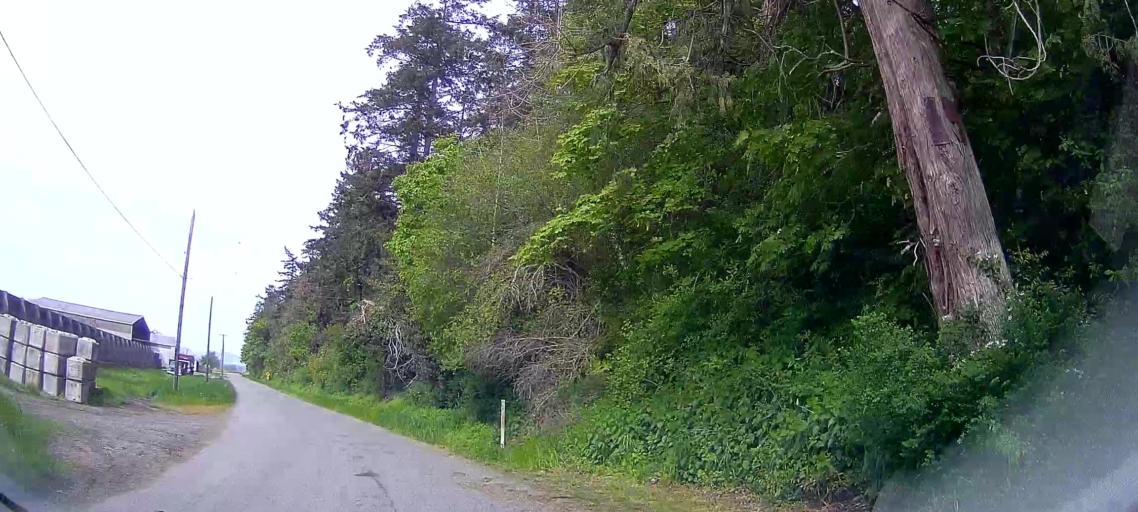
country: US
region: Washington
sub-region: Skagit County
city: Mount Vernon
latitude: 48.3919
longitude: -122.4495
